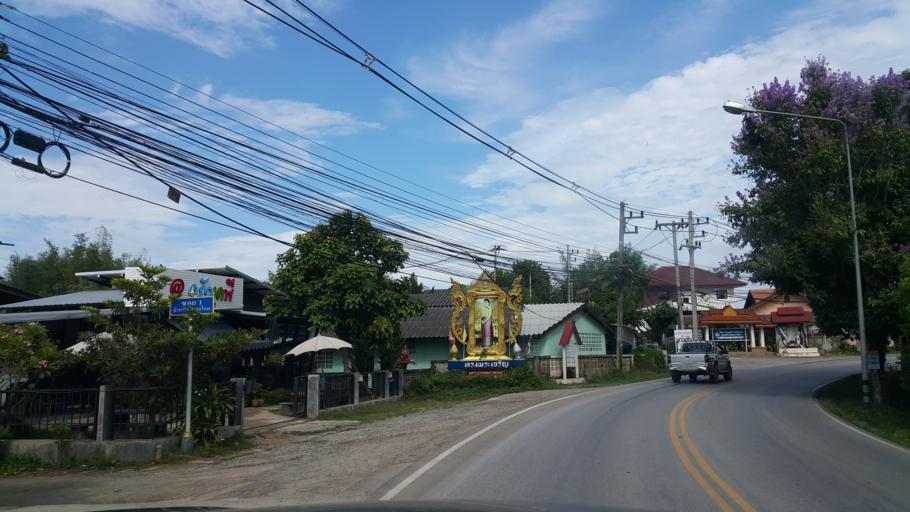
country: TH
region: Chiang Rai
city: Chiang Rai
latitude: 19.9118
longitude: 99.8767
